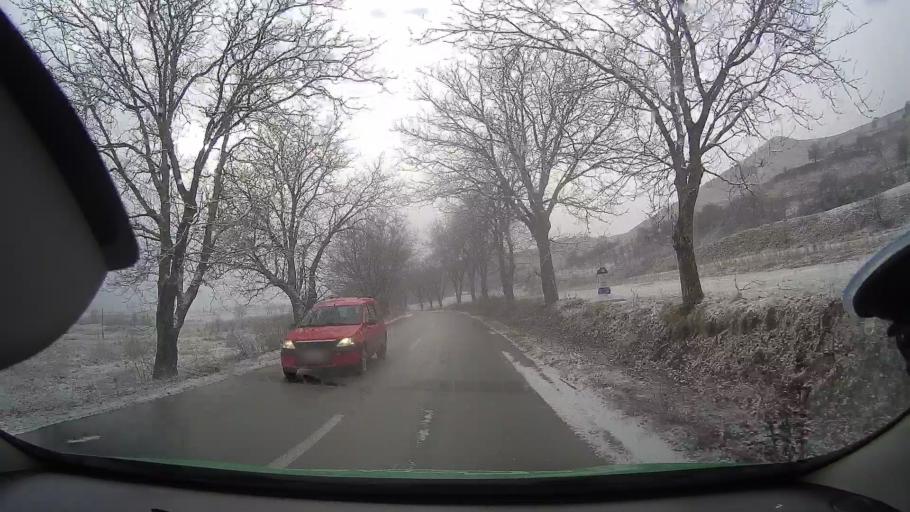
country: RO
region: Alba
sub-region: Comuna Rimetea
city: Rimetea
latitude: 46.4375
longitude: 23.5618
